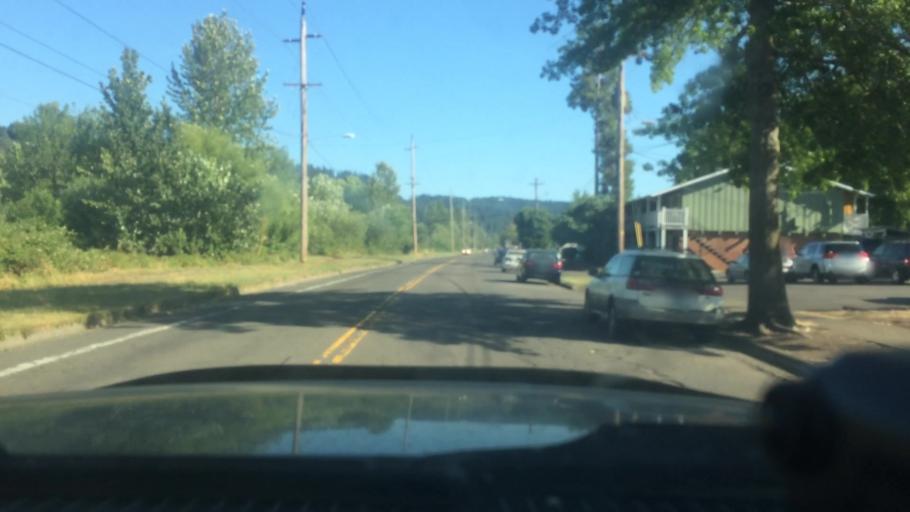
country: US
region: Oregon
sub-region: Lane County
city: Eugene
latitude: 44.0185
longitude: -123.0802
